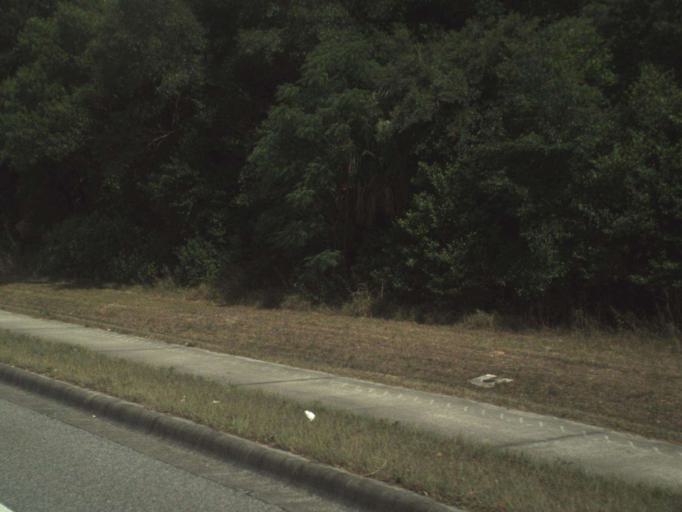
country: US
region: Florida
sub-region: Lake County
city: Mount Dora
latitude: 28.8228
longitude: -81.6619
